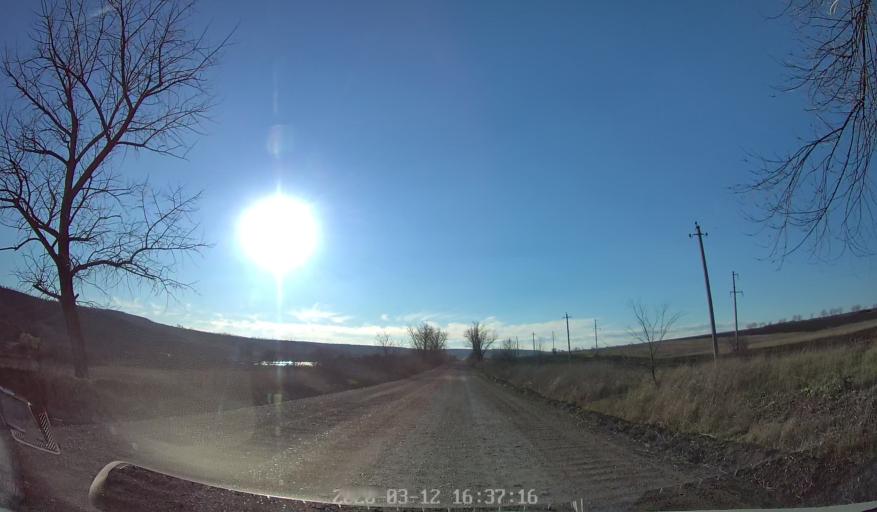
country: MD
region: Anenii Noi
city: Anenii Noi
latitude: 46.8153
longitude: 29.1899
